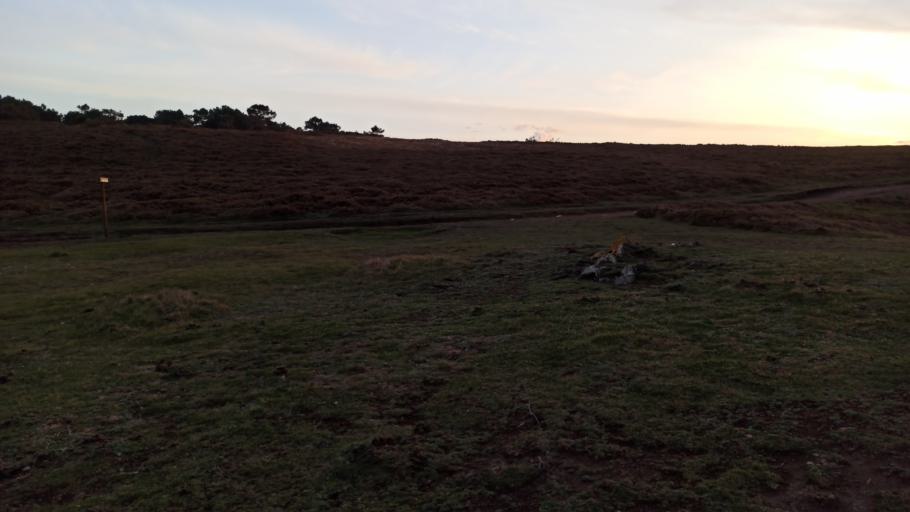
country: ES
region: Galicia
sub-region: Provincia da Coruna
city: A Coruna
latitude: 43.3967
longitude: -8.3461
